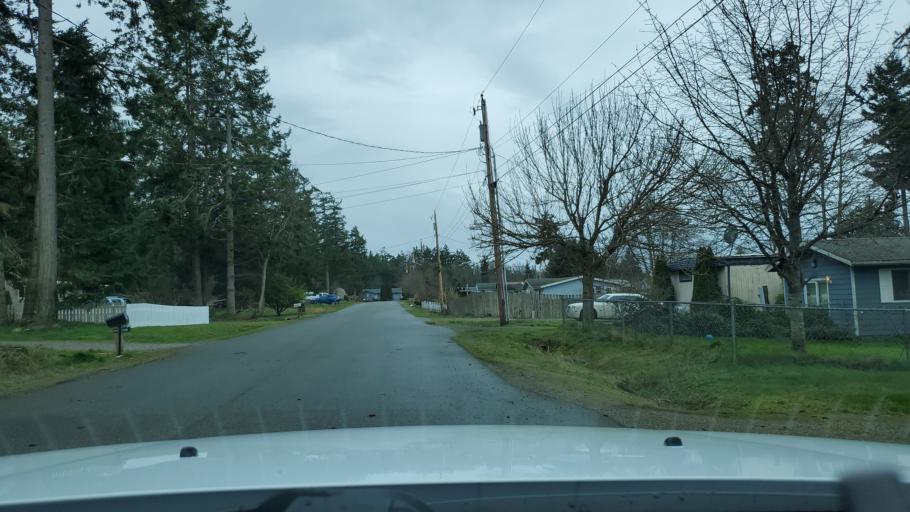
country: US
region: Washington
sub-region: Island County
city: Ault Field
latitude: 48.3680
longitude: -122.6428
